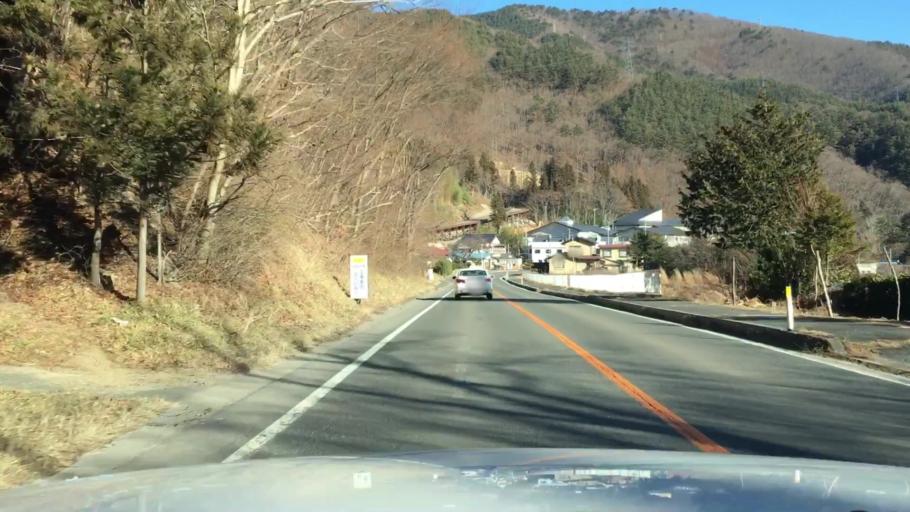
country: JP
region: Iwate
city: Miyako
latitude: 39.5966
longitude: 141.6770
